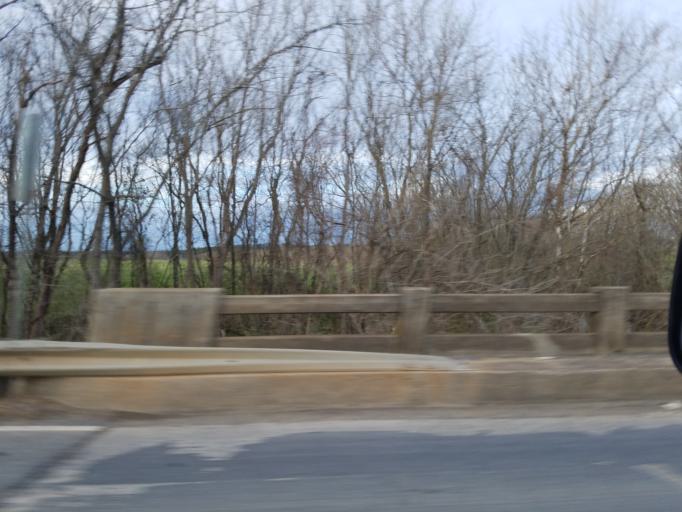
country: US
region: Georgia
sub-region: Bartow County
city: Rydal
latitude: 34.4347
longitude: -84.7156
